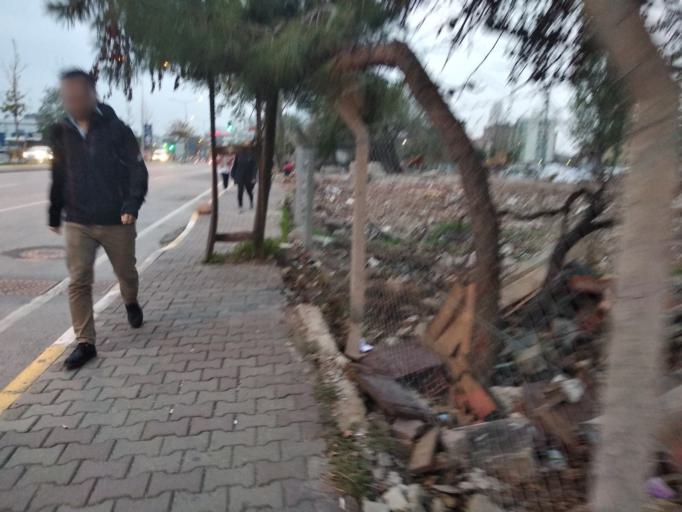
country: TR
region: Istanbul
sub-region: Atasehir
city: Atasehir
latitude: 40.9805
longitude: 29.1299
